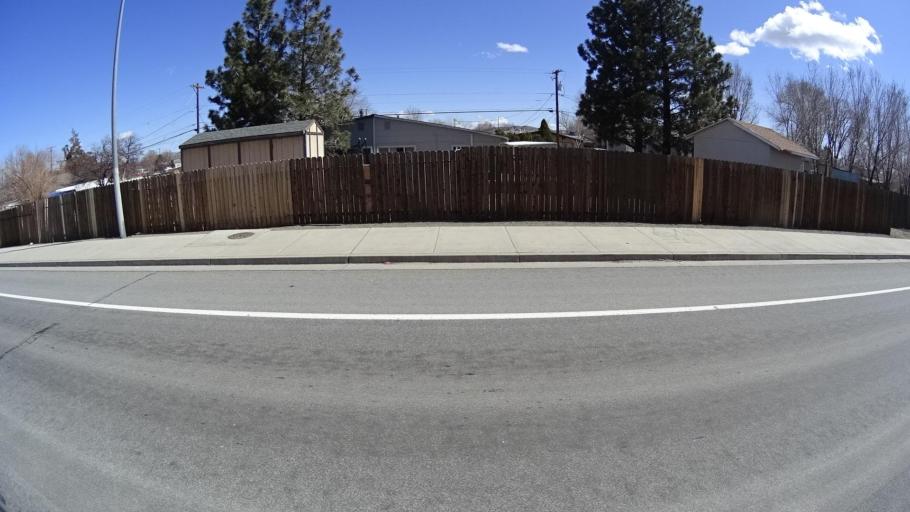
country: US
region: Nevada
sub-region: Washoe County
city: Lemmon Valley
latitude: 39.6344
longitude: -119.8819
